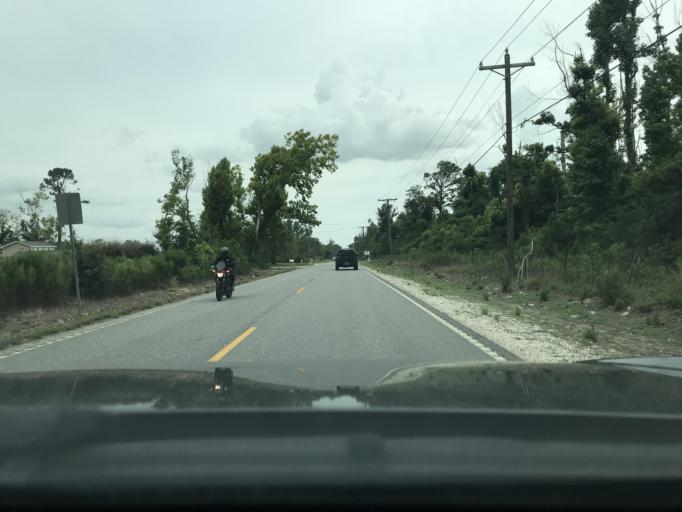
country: US
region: Louisiana
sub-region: Calcasieu Parish
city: Moss Bluff
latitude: 30.3167
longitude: -93.2583
